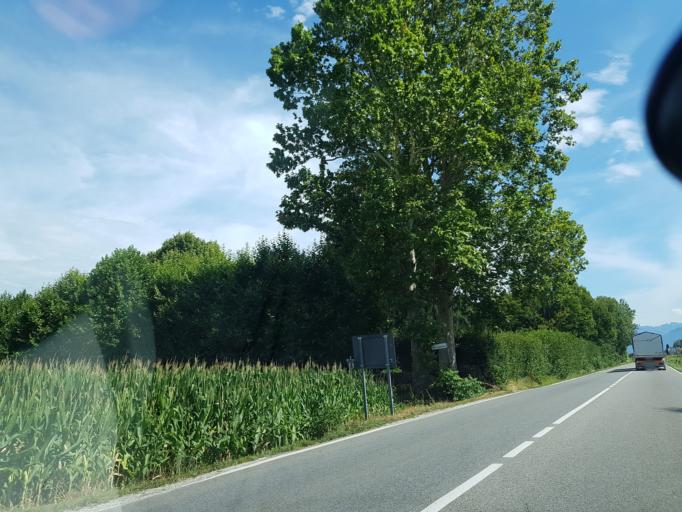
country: IT
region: Piedmont
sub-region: Provincia di Cuneo
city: Roata Rossi
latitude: 44.4455
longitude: 7.5288
